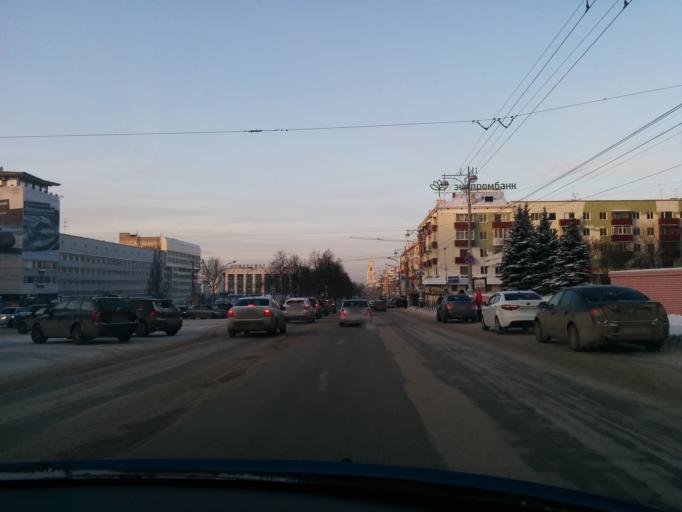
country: RU
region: Perm
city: Perm
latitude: 58.0086
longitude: 56.2417
